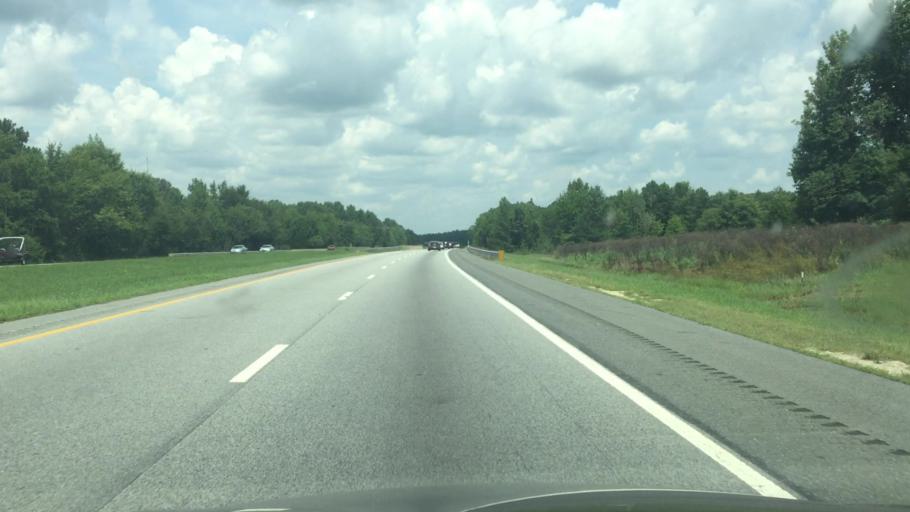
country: US
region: North Carolina
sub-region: Guilford County
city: Pleasant Garden
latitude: 35.9406
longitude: -79.8259
